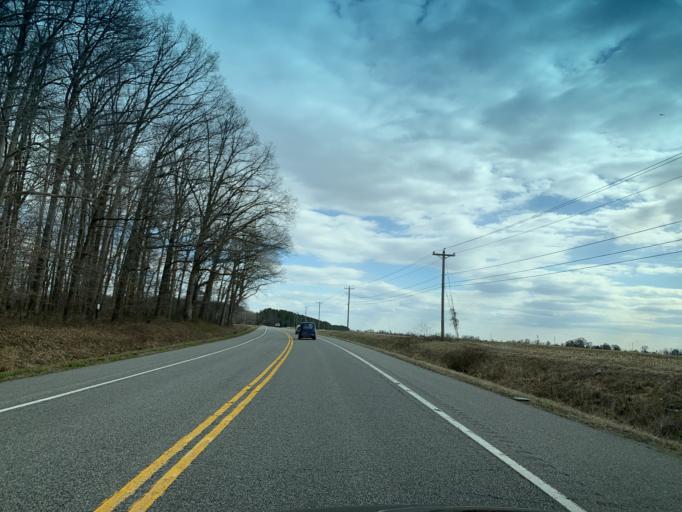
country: US
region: Maryland
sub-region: Queen Anne's County
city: Centreville
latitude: 38.9908
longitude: -76.0749
